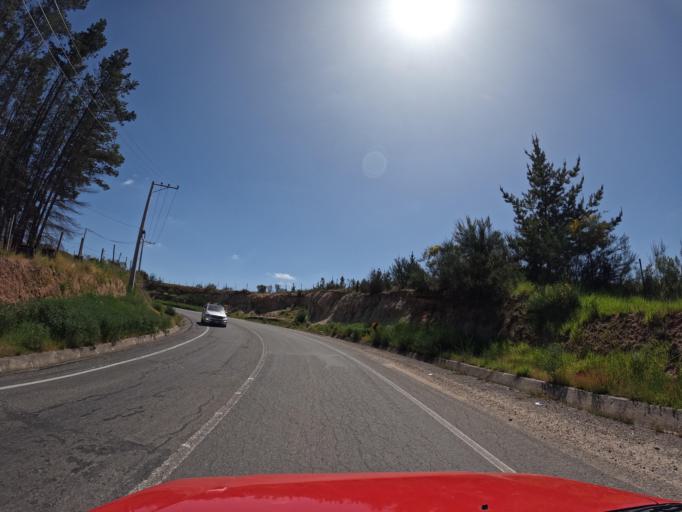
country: CL
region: O'Higgins
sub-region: Provincia de Colchagua
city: Santa Cruz
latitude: -34.6591
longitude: -71.8535
